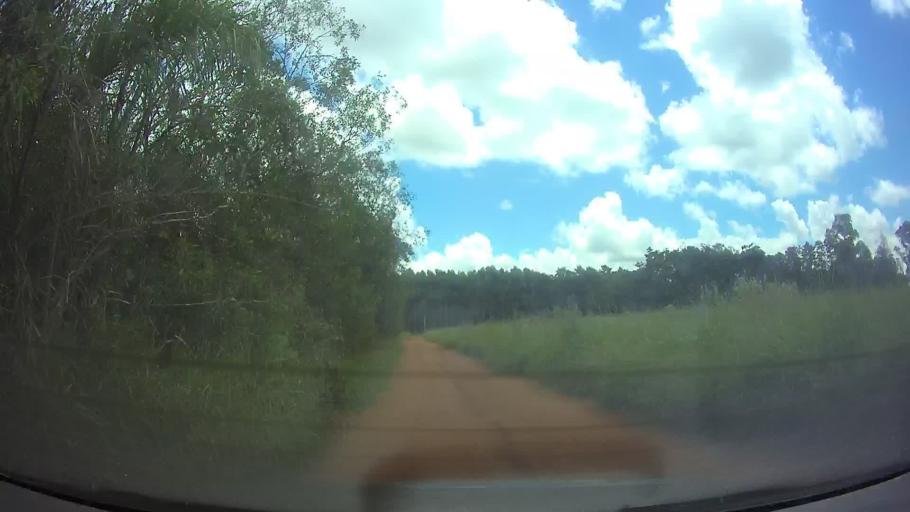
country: PY
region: Paraguari
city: La Colmena
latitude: -25.9643
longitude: -56.7362
